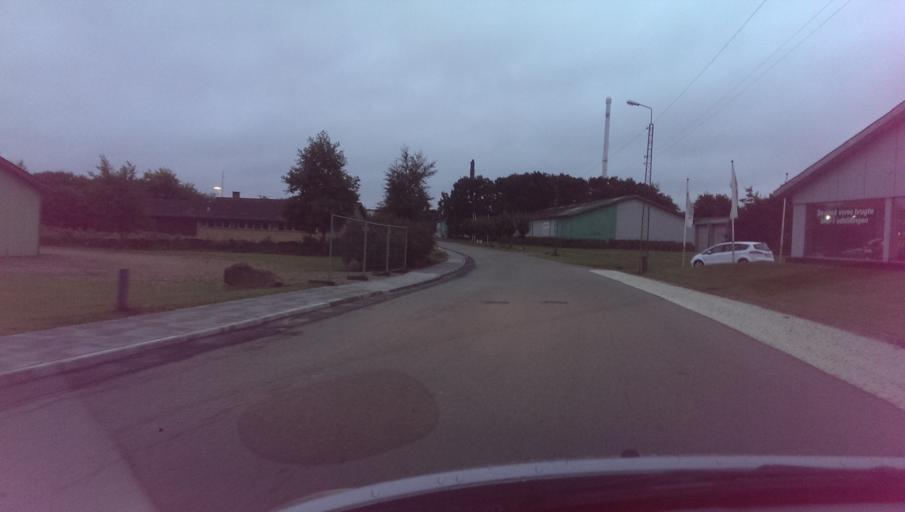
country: DK
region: South Denmark
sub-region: Varde Kommune
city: Olgod
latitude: 55.8145
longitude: 8.6259
